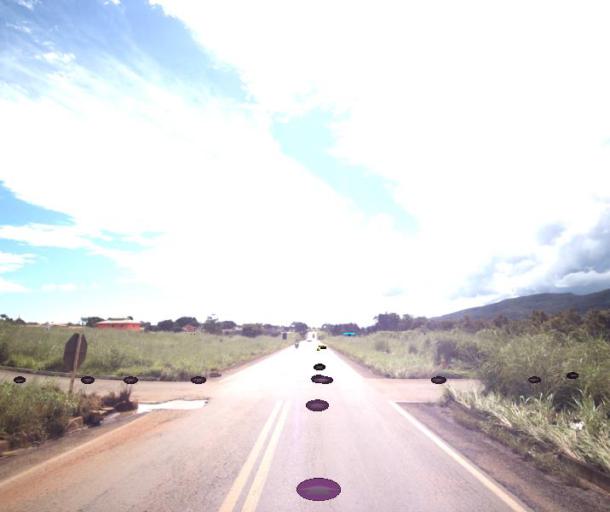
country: BR
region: Goias
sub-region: Pirenopolis
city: Pirenopolis
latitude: -16.0202
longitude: -49.1086
